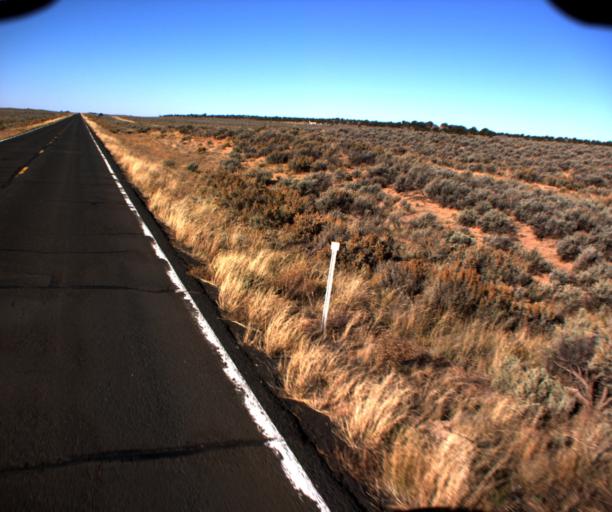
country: US
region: Arizona
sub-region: Navajo County
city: First Mesa
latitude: 35.7601
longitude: -110.0104
